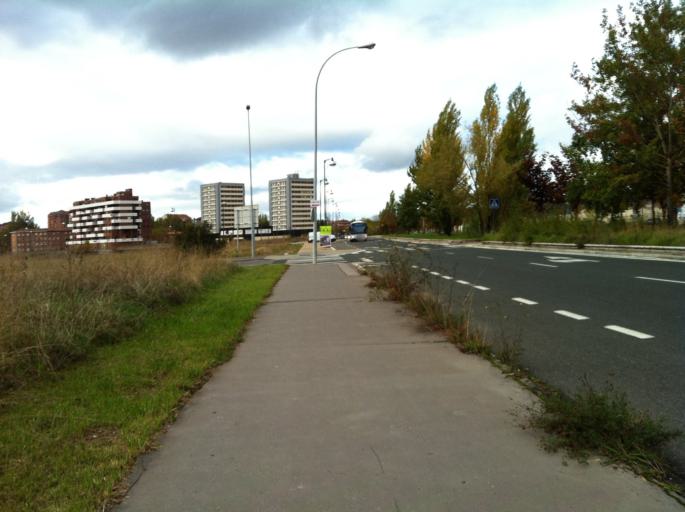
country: ES
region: Basque Country
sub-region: Provincia de Alava
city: Gasteiz / Vitoria
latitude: 42.8315
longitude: -2.6552
